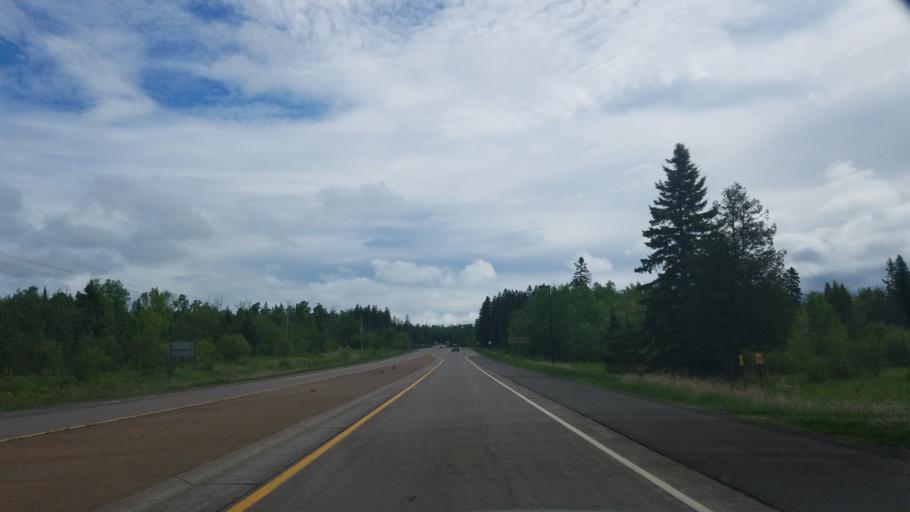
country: US
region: Minnesota
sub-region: Lake County
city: Two Harbors
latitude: 47.1376
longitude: -91.4764
